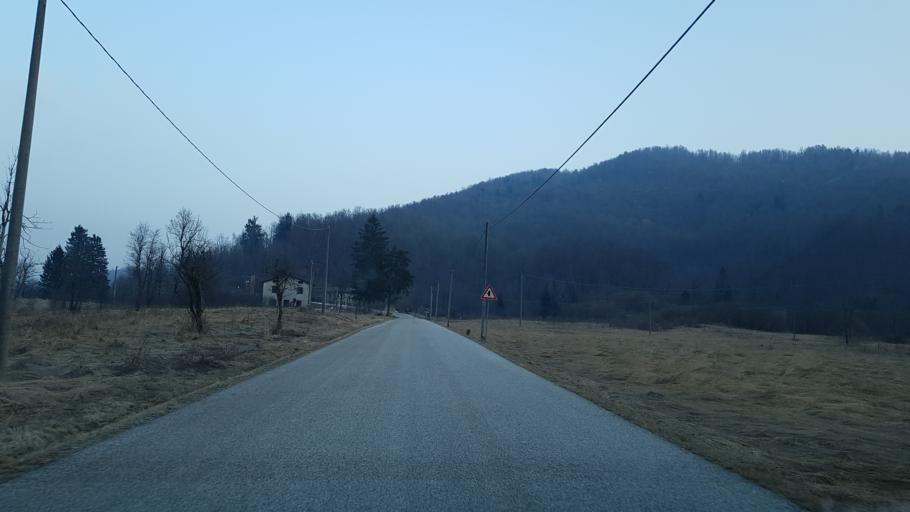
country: IT
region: Friuli Venezia Giulia
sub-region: Provincia di Udine
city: Taipana
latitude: 46.2551
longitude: 13.3639
